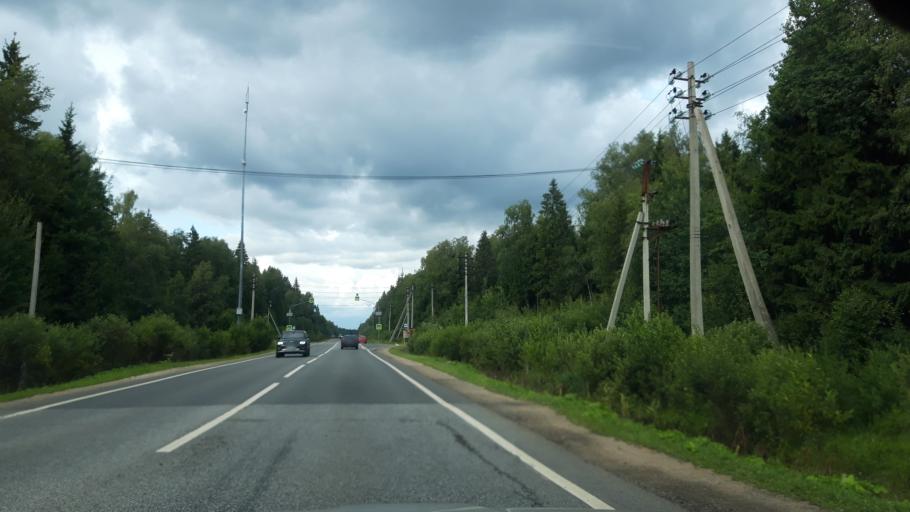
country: RU
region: Moskovskaya
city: Istra
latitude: 56.0537
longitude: 36.8964
